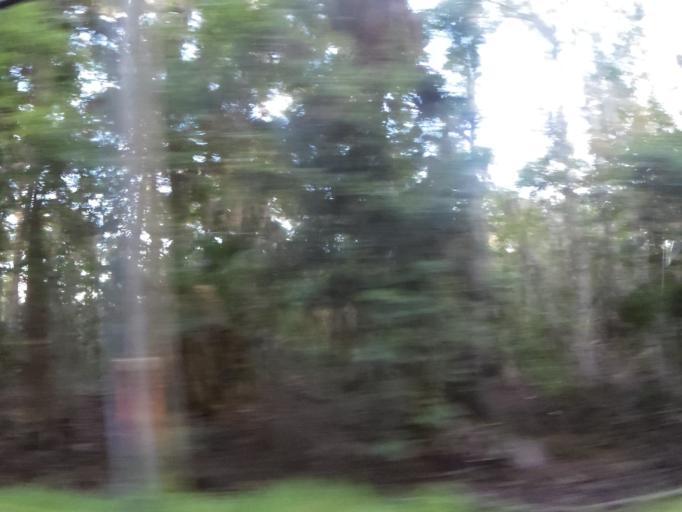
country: US
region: Florida
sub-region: Saint Johns County
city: Palm Valley
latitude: 30.1709
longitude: -81.3939
